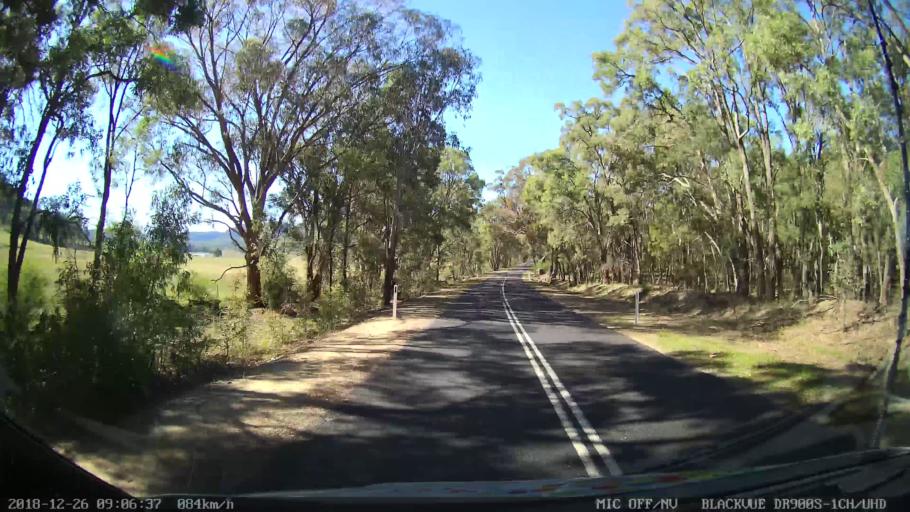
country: AU
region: New South Wales
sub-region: Mid-Western Regional
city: Kandos
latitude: -32.6963
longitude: 150.0059
